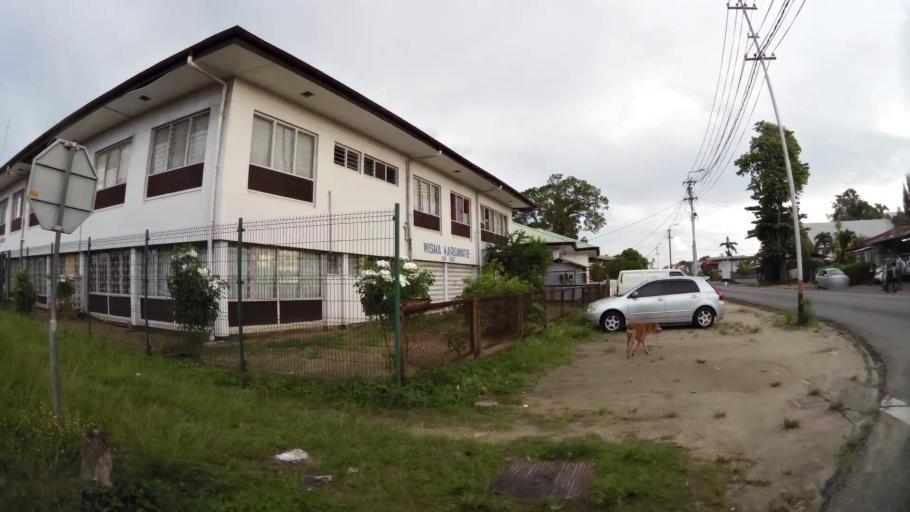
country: SR
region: Paramaribo
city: Paramaribo
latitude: 5.8326
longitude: -55.1488
